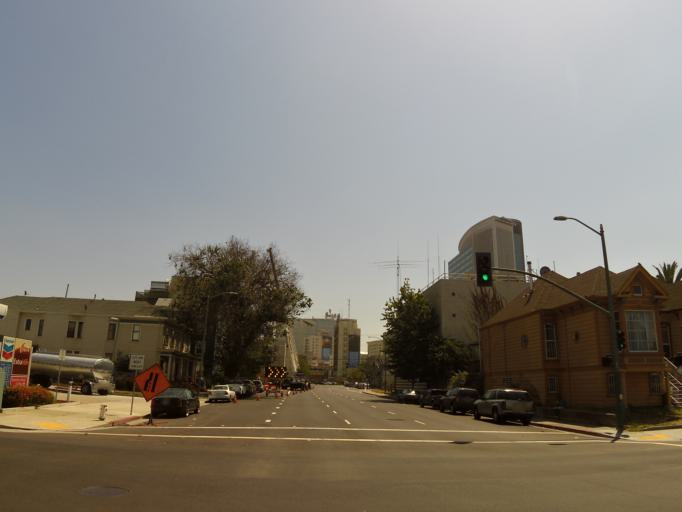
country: US
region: California
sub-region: Alameda County
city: Oakland
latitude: 37.8087
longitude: -122.2760
